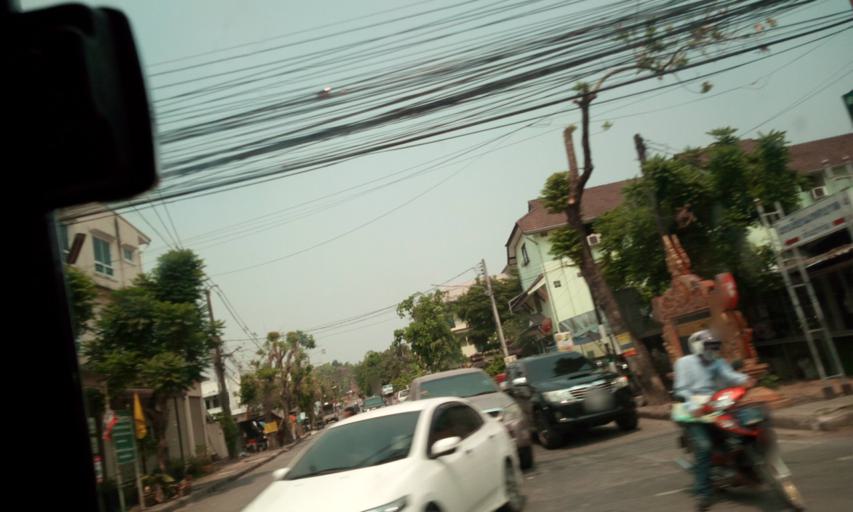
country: TH
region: Chiang Rai
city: Chiang Rai
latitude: 19.8858
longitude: 99.8306
